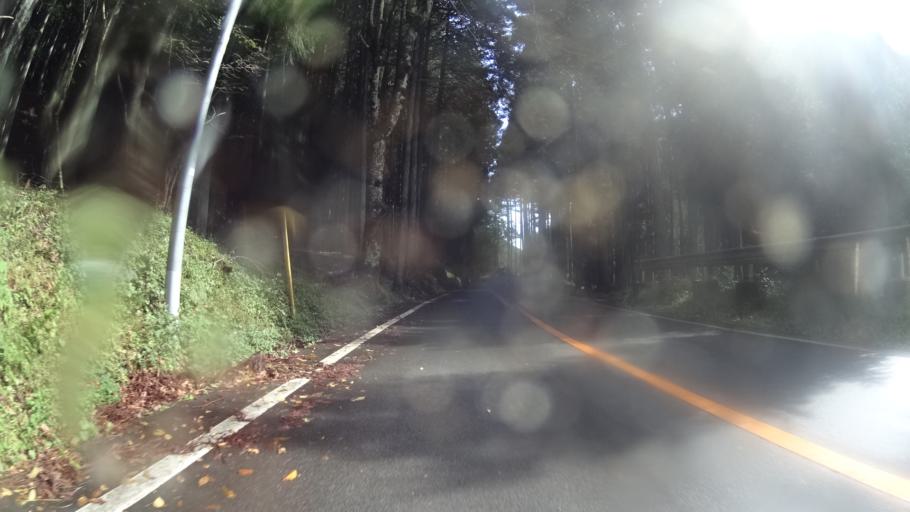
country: JP
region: Yamanashi
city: Enzan
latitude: 35.7942
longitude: 138.9023
